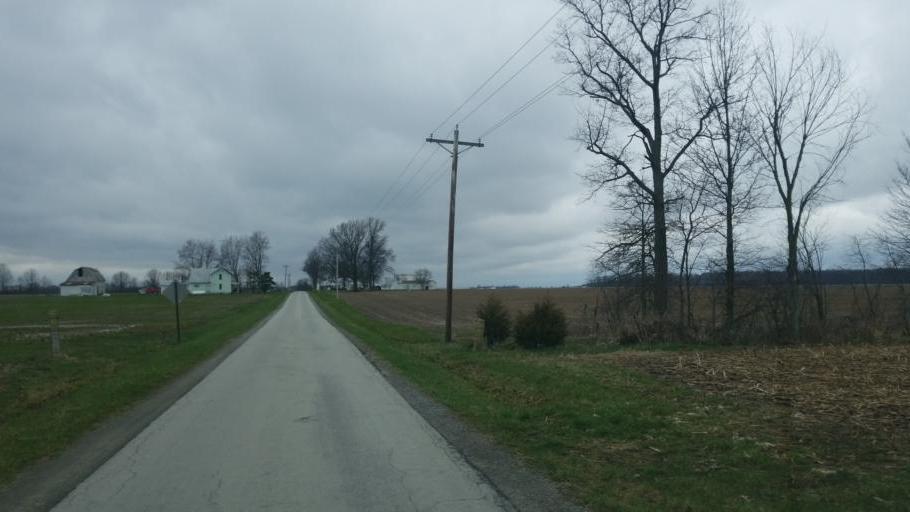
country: US
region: Ohio
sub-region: Hardin County
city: Forest
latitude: 40.7377
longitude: -83.4340
